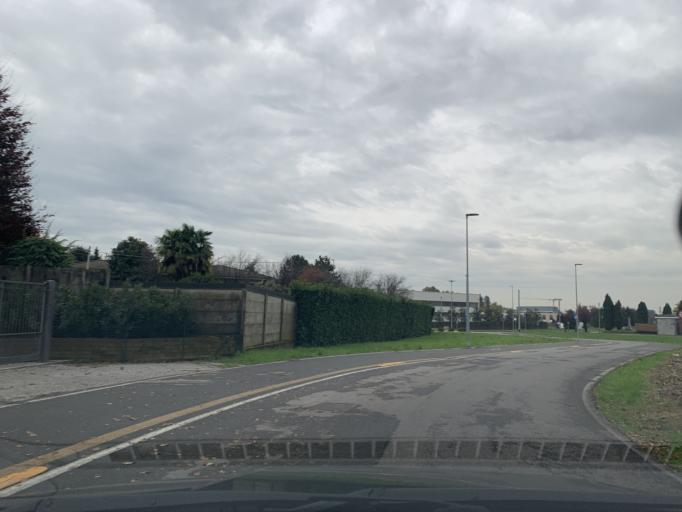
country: IT
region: Lombardy
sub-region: Provincia di Como
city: Puginate
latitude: 45.7099
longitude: 9.0558
